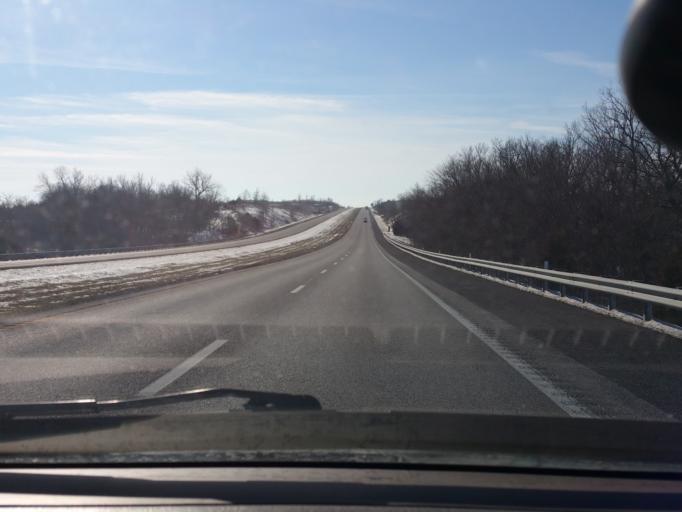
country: US
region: Missouri
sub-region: Daviess County
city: Gallatin
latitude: 39.9155
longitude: -94.1431
